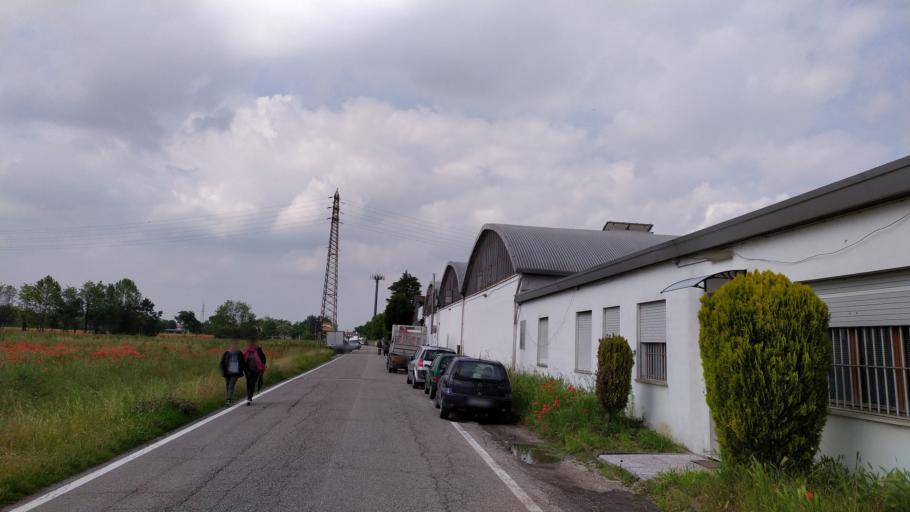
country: IT
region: Veneto
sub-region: Provincia di Padova
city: Vigodarzere
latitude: 45.4533
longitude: 11.8941
